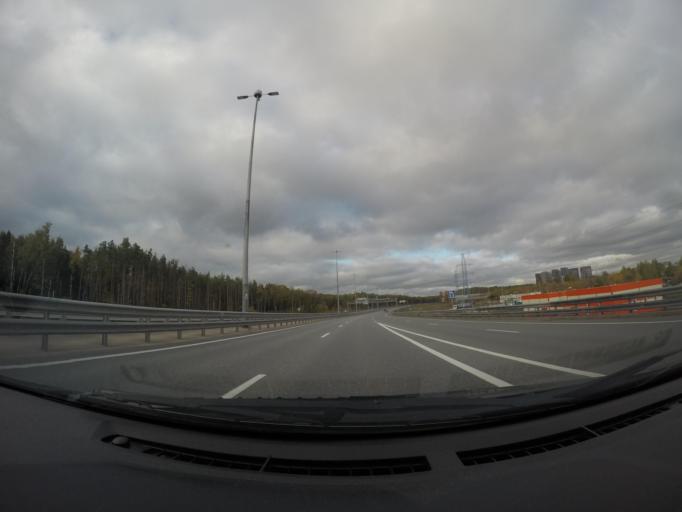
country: RU
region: Moskovskaya
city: Lesnoy Gorodok
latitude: 55.6695
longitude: 37.2244
